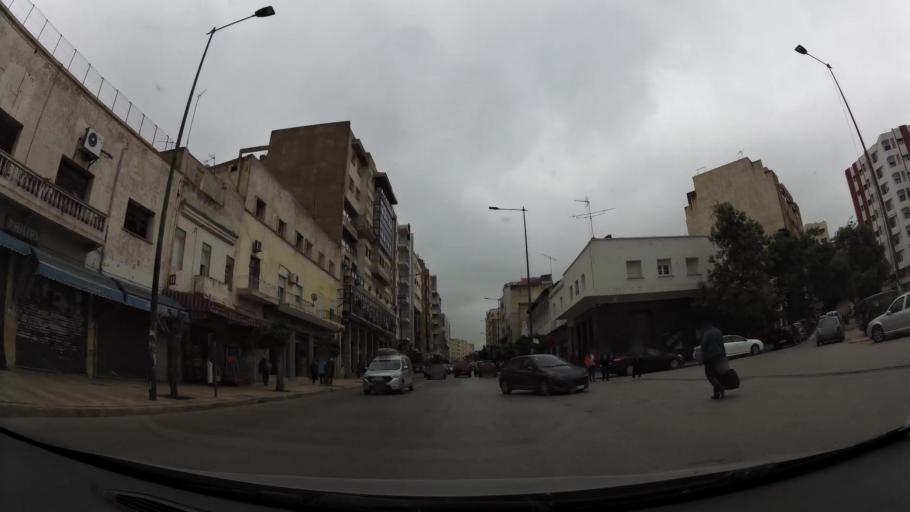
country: MA
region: Fes-Boulemane
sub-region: Fes
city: Fes
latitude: 34.0357
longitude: -4.9976
